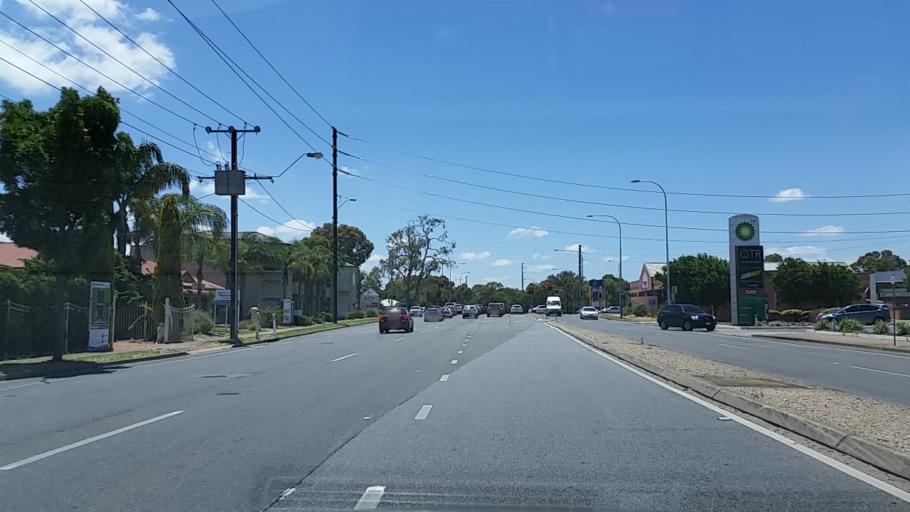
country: AU
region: South Australia
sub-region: Salisbury
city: Salisbury
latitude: -34.7647
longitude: 138.6394
